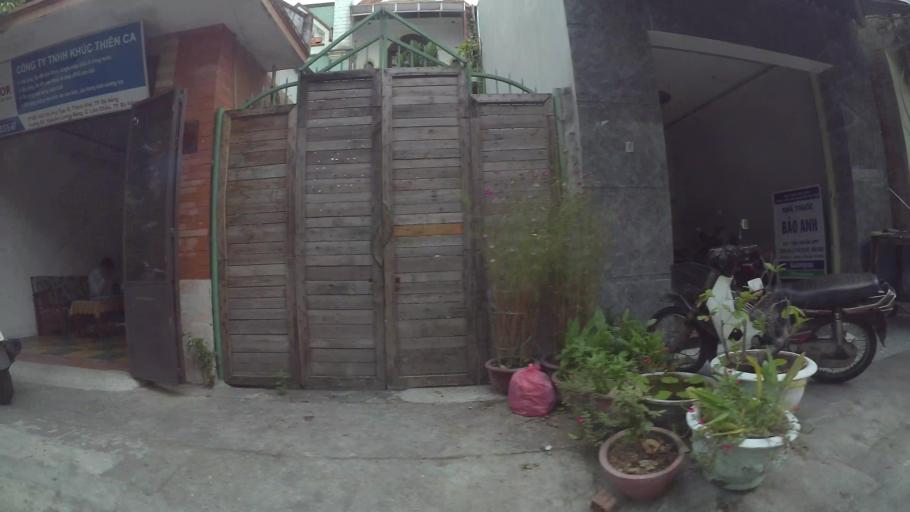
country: VN
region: Da Nang
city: Thanh Khe
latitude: 16.0686
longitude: 108.1916
